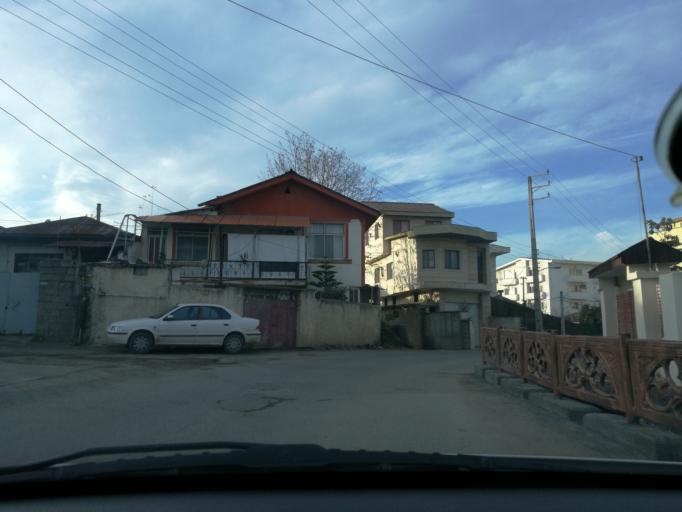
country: IR
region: Mazandaran
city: Chalus
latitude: 36.6454
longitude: 51.4306
